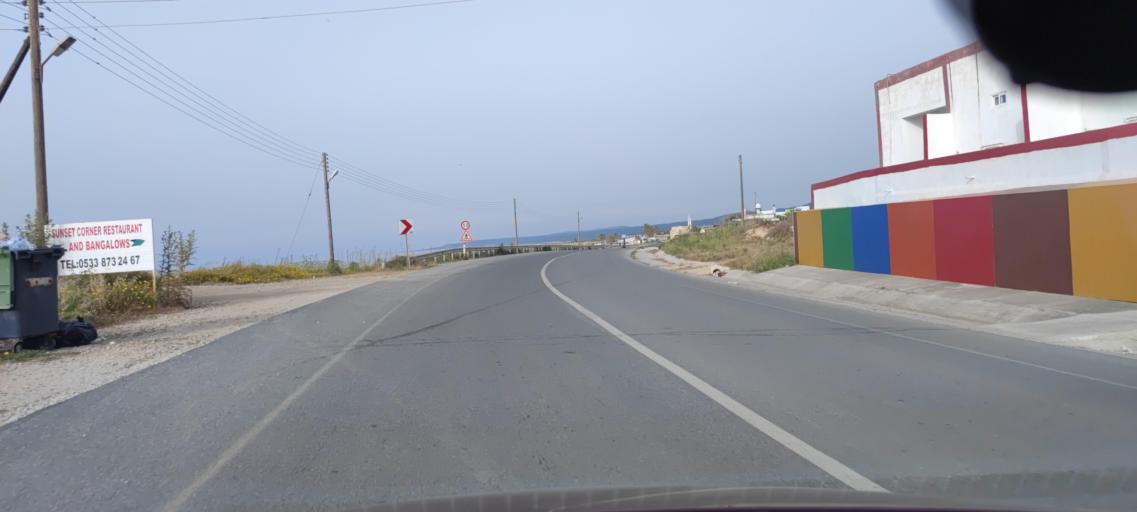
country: CY
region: Ammochostos
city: Rizokarpaso
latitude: 35.5689
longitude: 34.2517
